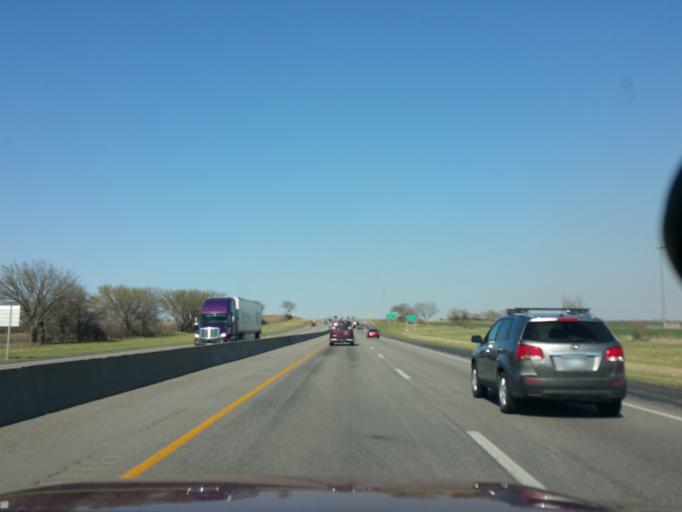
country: US
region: Kansas
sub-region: Leavenworth County
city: Tonganoxie
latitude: 39.0378
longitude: -95.1042
